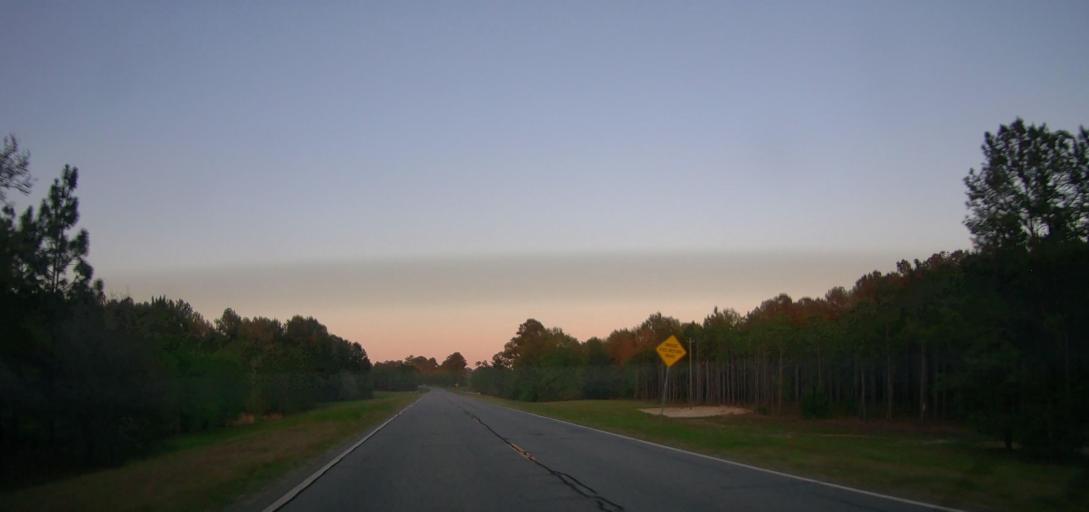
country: US
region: Georgia
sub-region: Wilcox County
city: Rochelle
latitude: 31.8168
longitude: -83.4720
